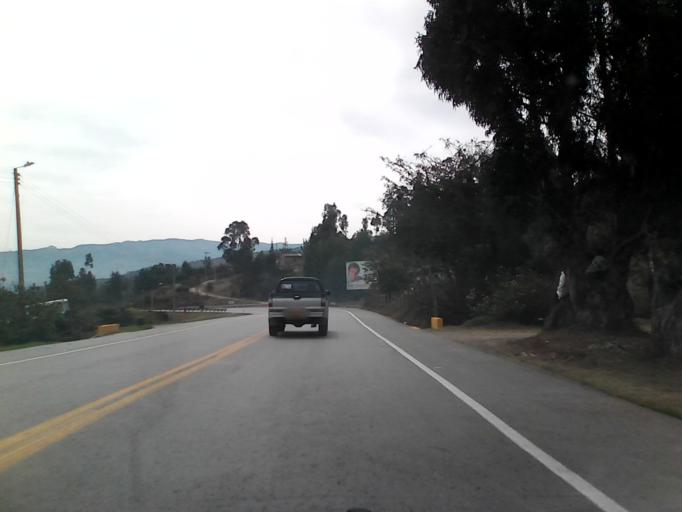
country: CO
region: Boyaca
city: Tibasosa
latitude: 5.7386
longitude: -72.9729
